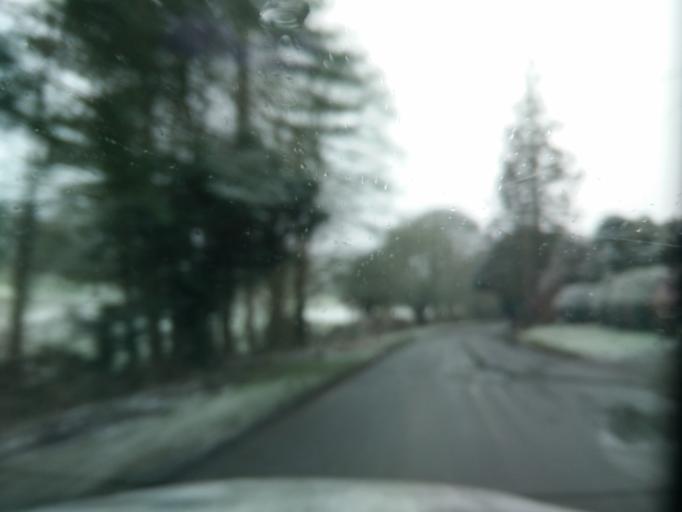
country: GB
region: England
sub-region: Buckinghamshire
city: Princes Risborough
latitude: 51.7353
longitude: -0.8079
